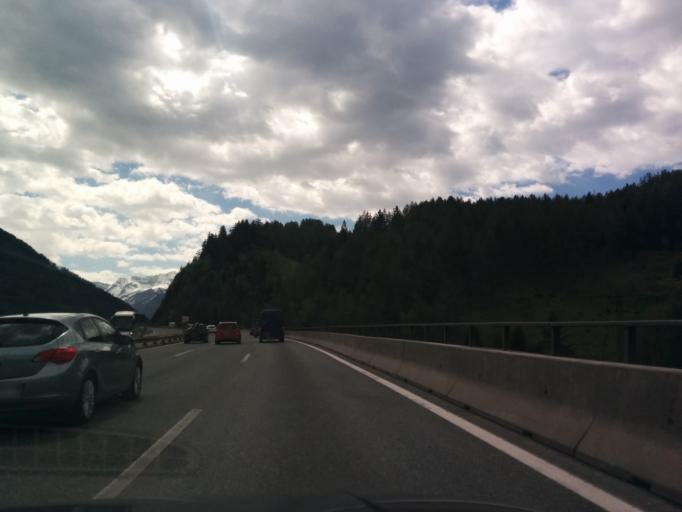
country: AT
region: Tyrol
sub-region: Politischer Bezirk Innsbruck Land
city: Steinach am Brenner
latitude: 47.0780
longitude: 11.4717
